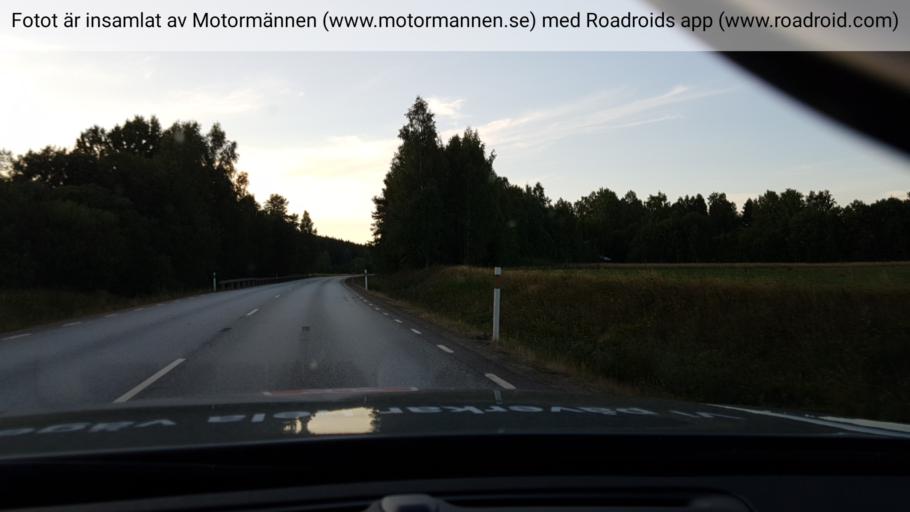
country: SE
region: Vaermland
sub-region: Storfors Kommun
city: Storfors
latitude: 59.5108
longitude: 14.3053
